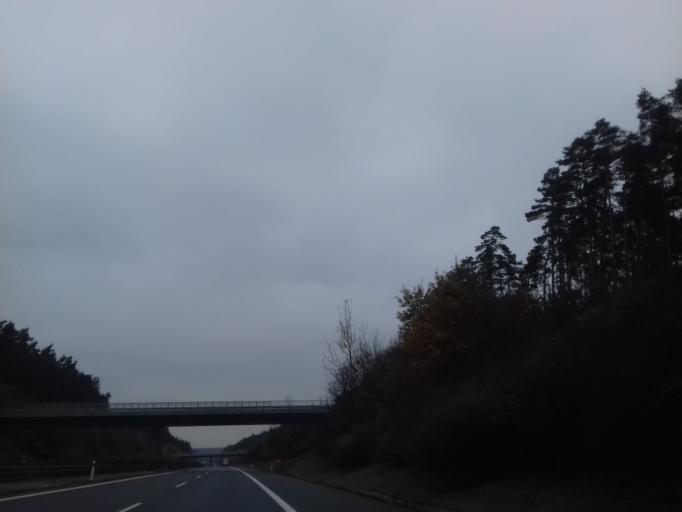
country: CZ
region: Plzensky
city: Dobrany
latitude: 49.6860
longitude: 13.3011
